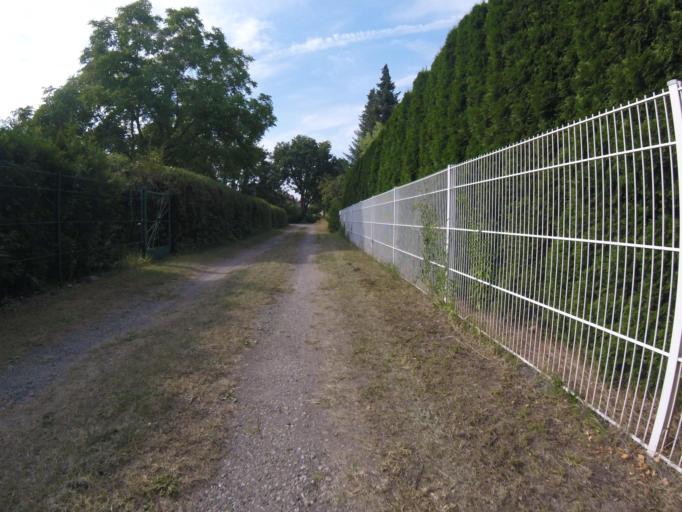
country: DE
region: Brandenburg
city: Spreenhagen
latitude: 52.2714
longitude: 13.8183
